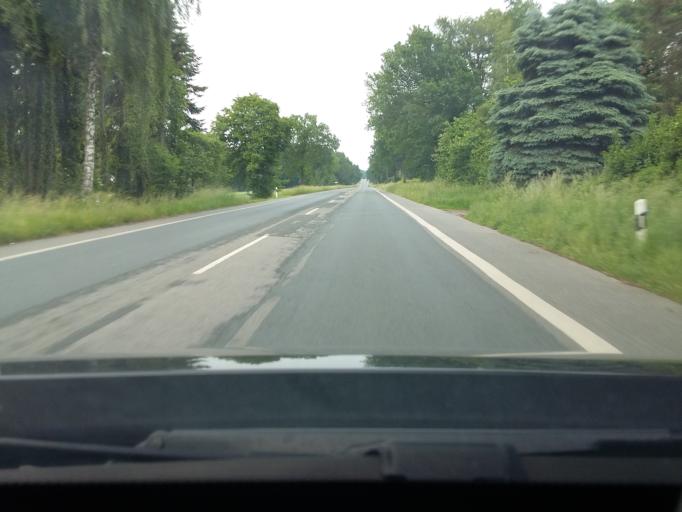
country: DE
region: North Rhine-Westphalia
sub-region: Regierungsbezirk Detmold
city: Vlotho
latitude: 52.1240
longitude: 8.8214
